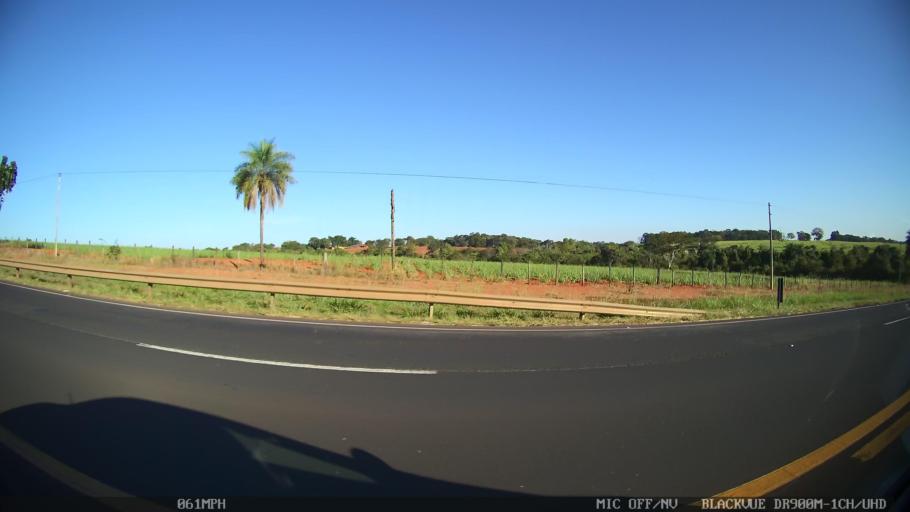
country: BR
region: Sao Paulo
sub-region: Guapiacu
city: Guapiacu
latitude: -20.7557
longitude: -49.1560
